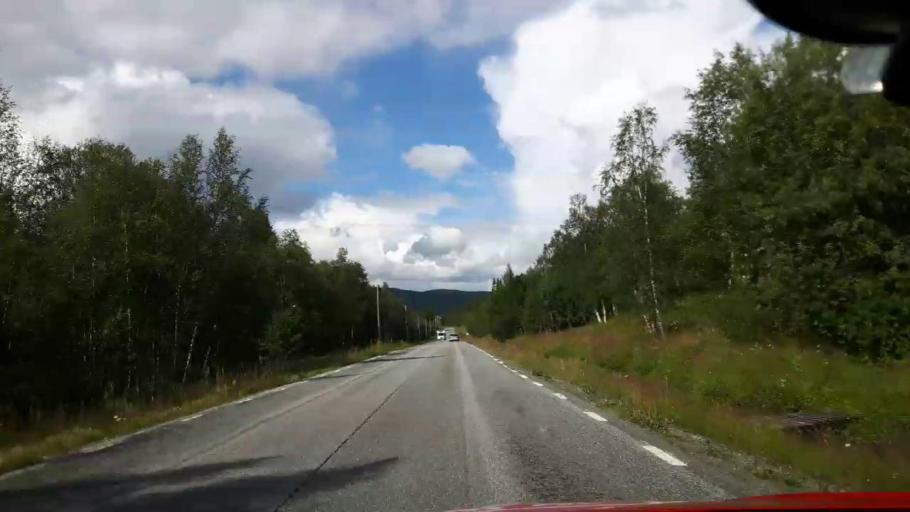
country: NO
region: Nordland
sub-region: Hattfjelldal
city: Hattfjelldal
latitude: 65.0619
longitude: 14.8838
